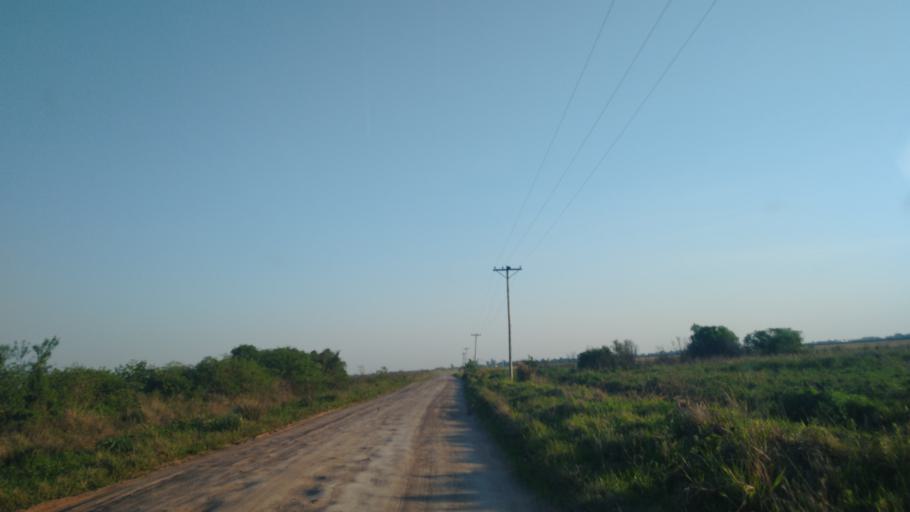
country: PY
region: Neembucu
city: Cerrito
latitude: -27.3915
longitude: -57.6586
